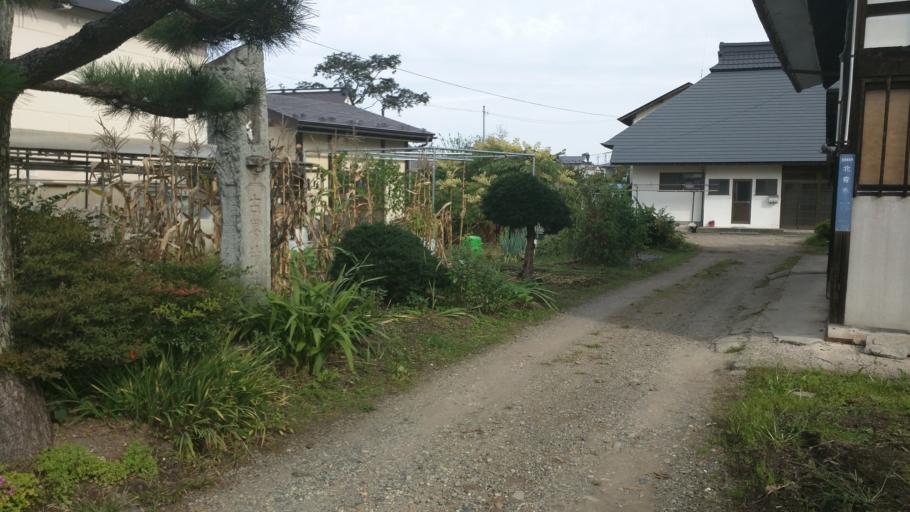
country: JP
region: Fukushima
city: Kitakata
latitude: 37.4801
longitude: 139.9396
